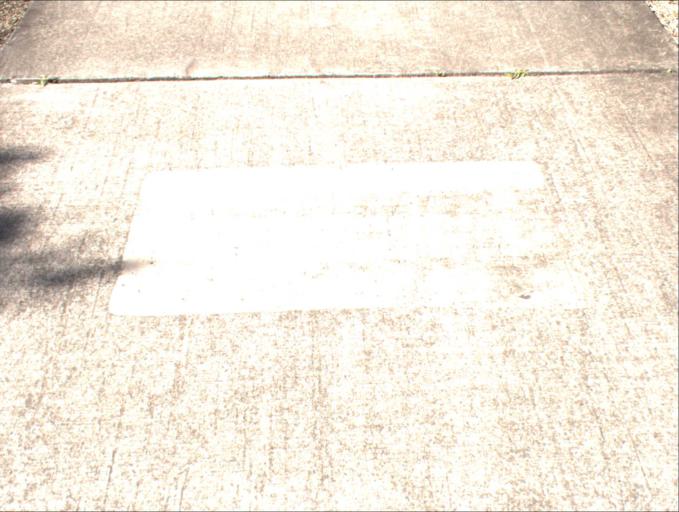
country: AU
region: Queensland
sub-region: Logan
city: Waterford West
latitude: -27.7083
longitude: 153.1610
